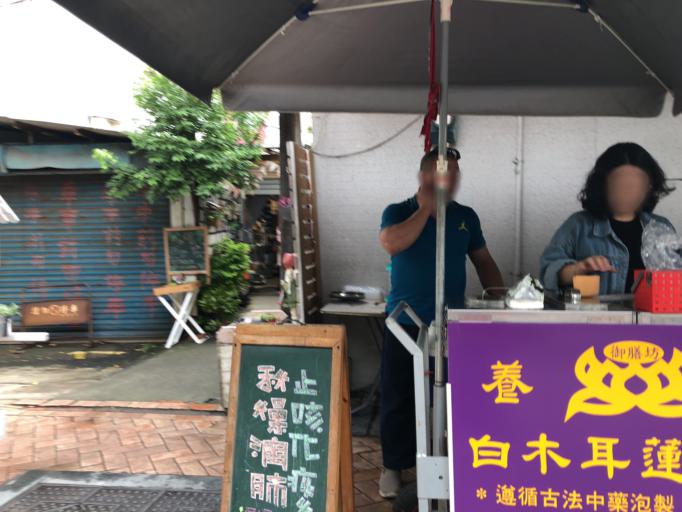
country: TW
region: Taiwan
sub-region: Taoyuan
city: Taoyuan
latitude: 24.9517
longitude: 121.3474
